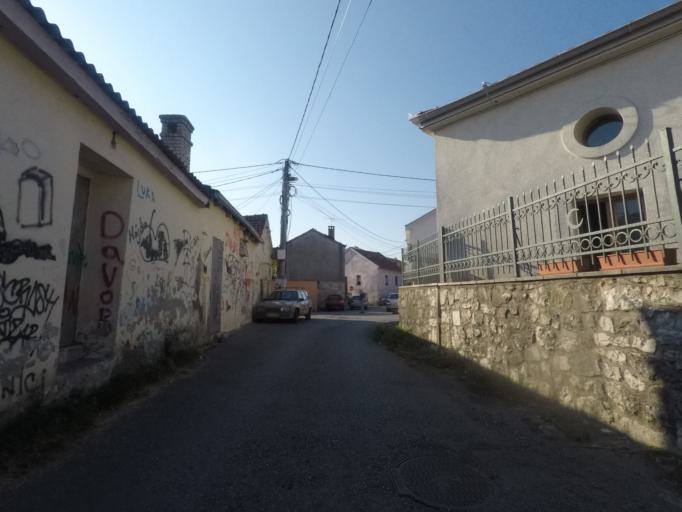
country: ME
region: Podgorica
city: Podgorica
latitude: 42.4377
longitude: 19.2592
